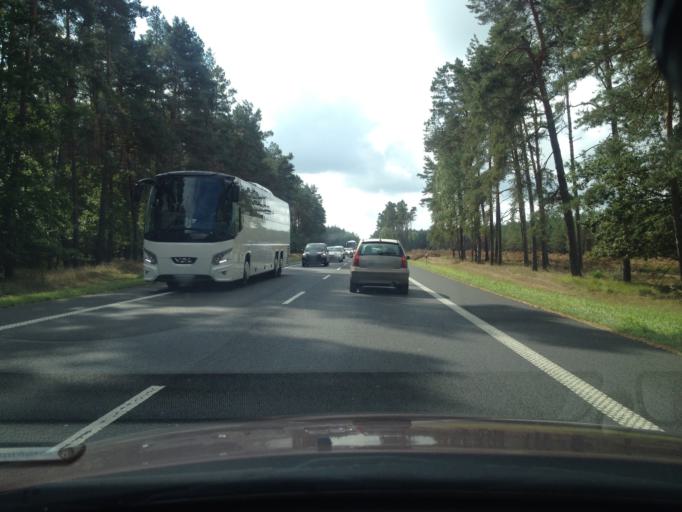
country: PL
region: West Pomeranian Voivodeship
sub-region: Powiat goleniowski
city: Goleniow
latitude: 53.6485
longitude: 14.8165
